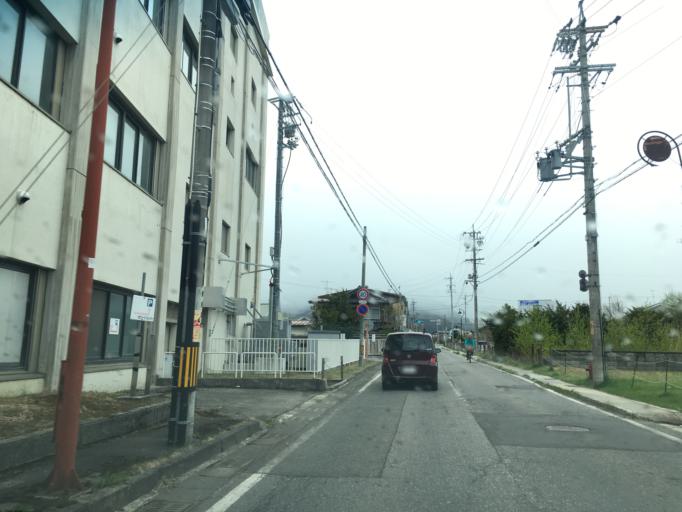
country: JP
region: Nagano
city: Omachi
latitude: 36.5105
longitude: 137.8531
